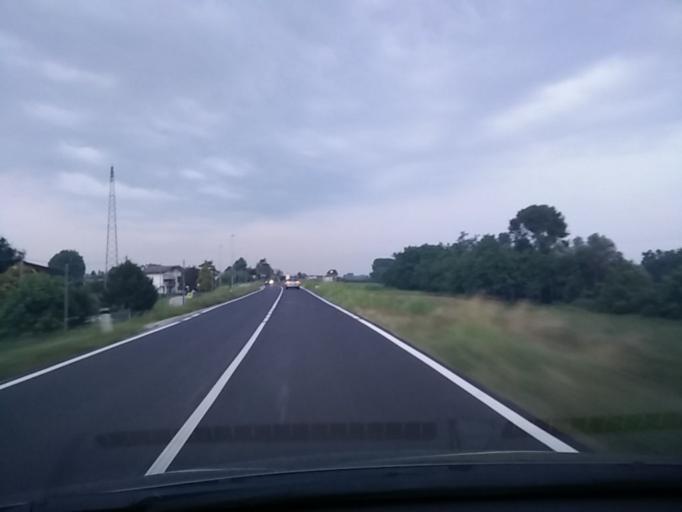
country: IT
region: Veneto
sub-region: Provincia di Venezia
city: Passarella
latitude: 45.5886
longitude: 12.6376
